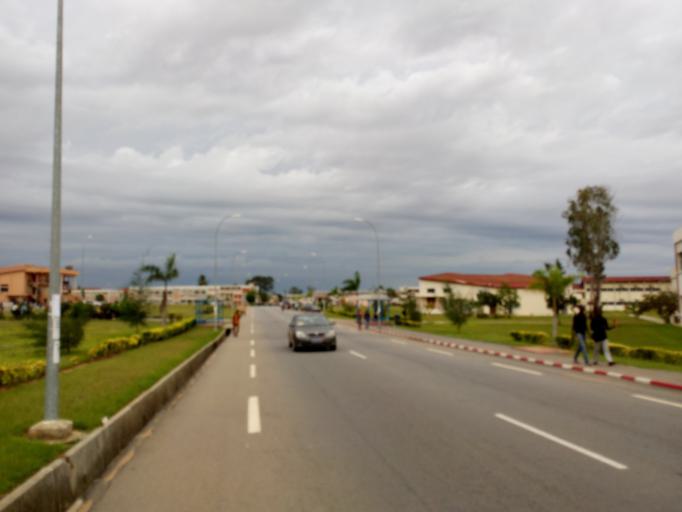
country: CI
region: Lagunes
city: Abidjan
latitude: 5.3492
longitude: -3.9885
